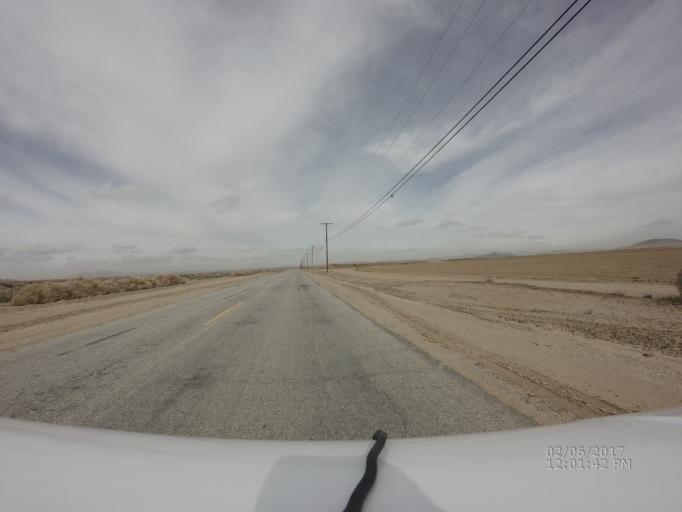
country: US
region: California
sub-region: Los Angeles County
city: Lake Los Angeles
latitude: 34.5688
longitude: -117.7026
